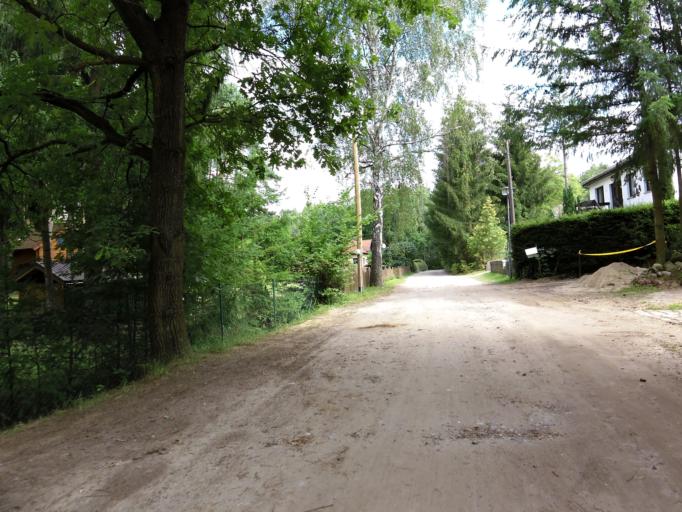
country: DE
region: Brandenburg
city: Lychen
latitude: 53.2219
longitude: 13.2791
